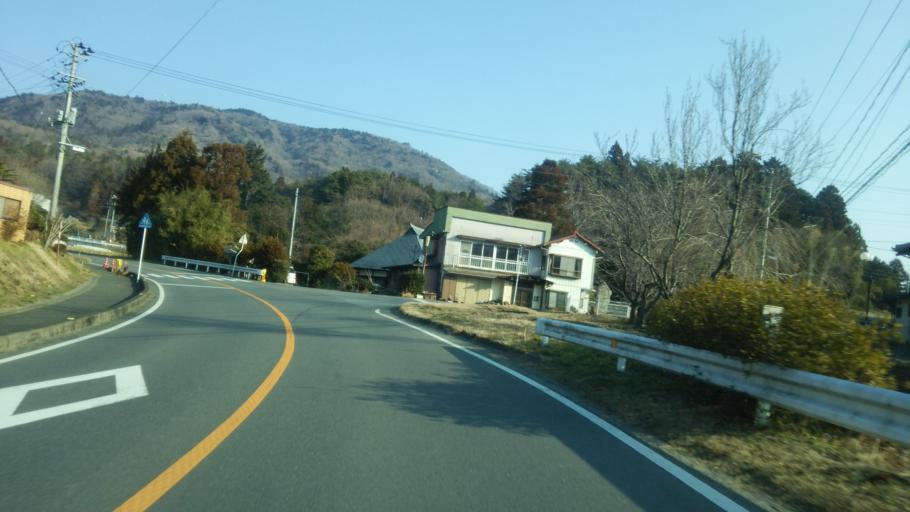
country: JP
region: Fukushima
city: Iwaki
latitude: 37.0791
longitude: 140.8054
